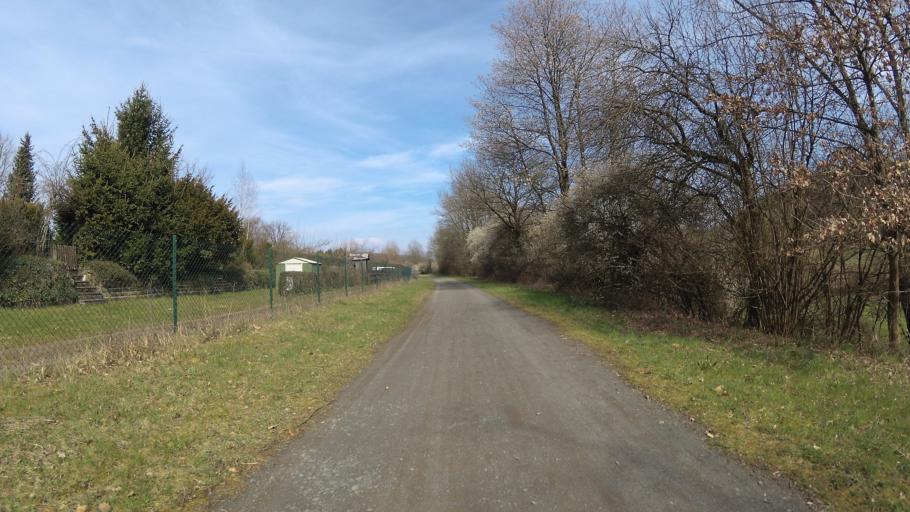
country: DE
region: Rheinland-Pfalz
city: Nanzdietschweiler
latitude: 49.4325
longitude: 7.4369
